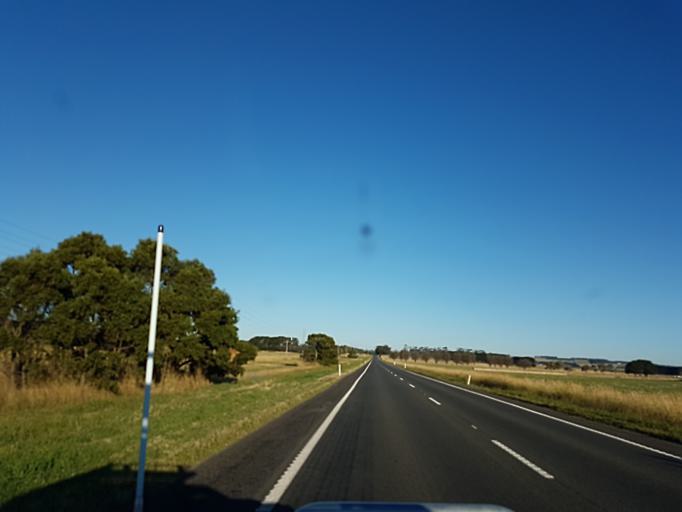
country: AU
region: Victoria
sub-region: Warrnambool
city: Allansford
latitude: -38.2175
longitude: 143.0323
